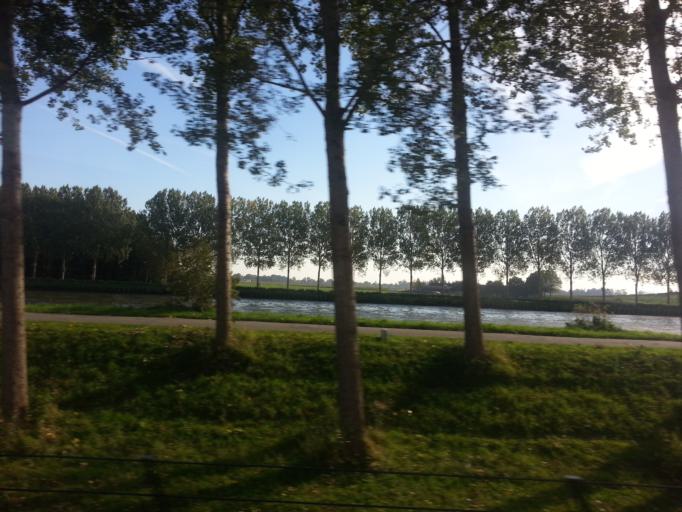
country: NL
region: Utrecht
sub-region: Stichtse Vecht
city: Vreeland
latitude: 52.2279
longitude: 5.0059
